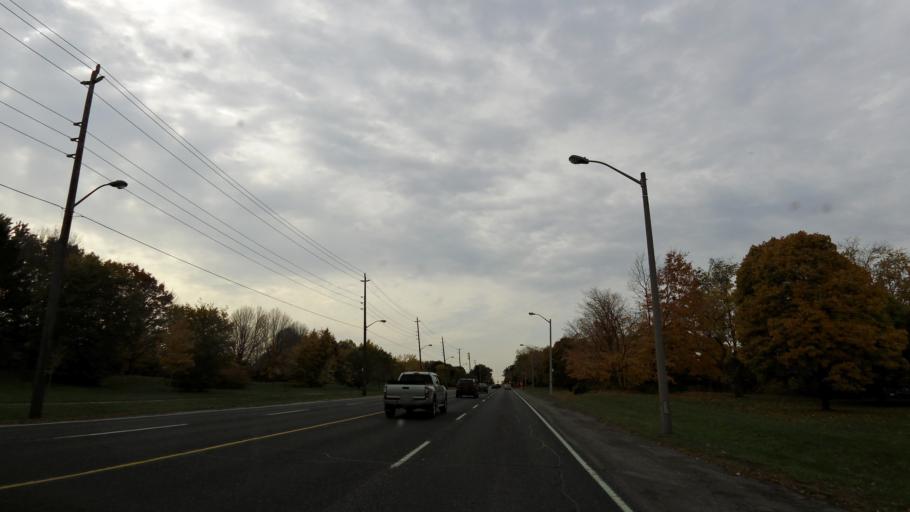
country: CA
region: Ontario
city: Etobicoke
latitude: 43.6810
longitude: -79.5348
